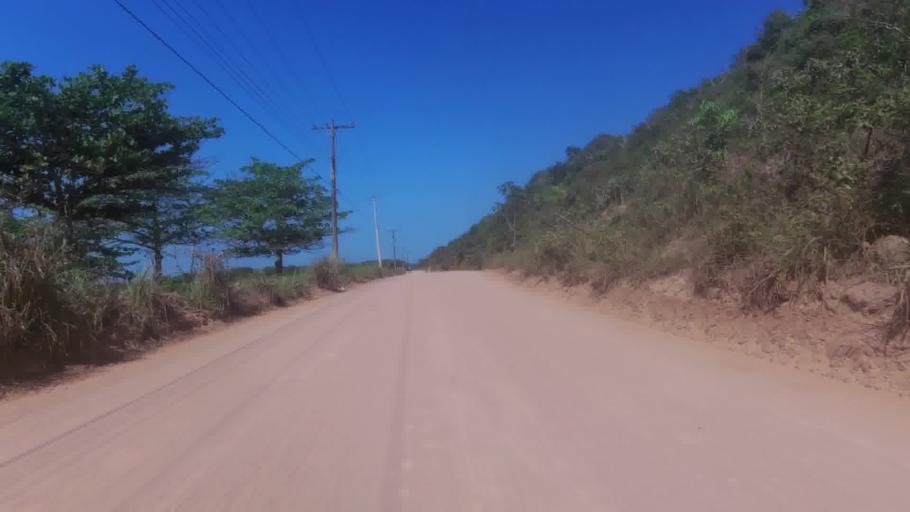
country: BR
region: Espirito Santo
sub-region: Marataizes
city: Marataizes
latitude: -21.0795
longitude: -40.8418
